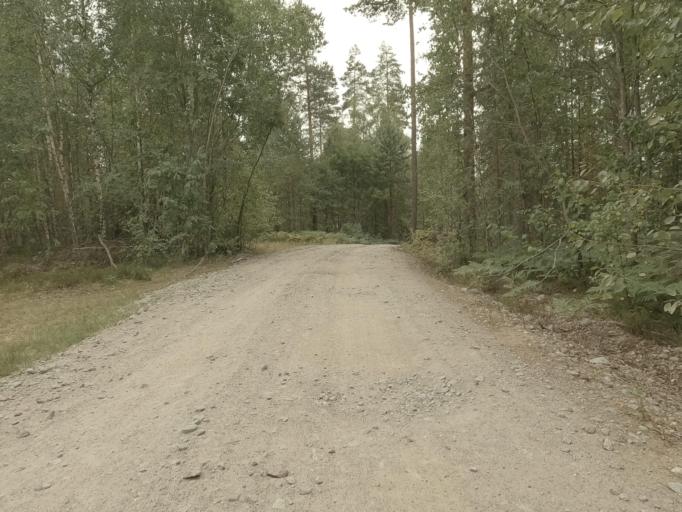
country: RU
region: Leningrad
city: Kamennogorsk
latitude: 60.9883
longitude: 29.1849
